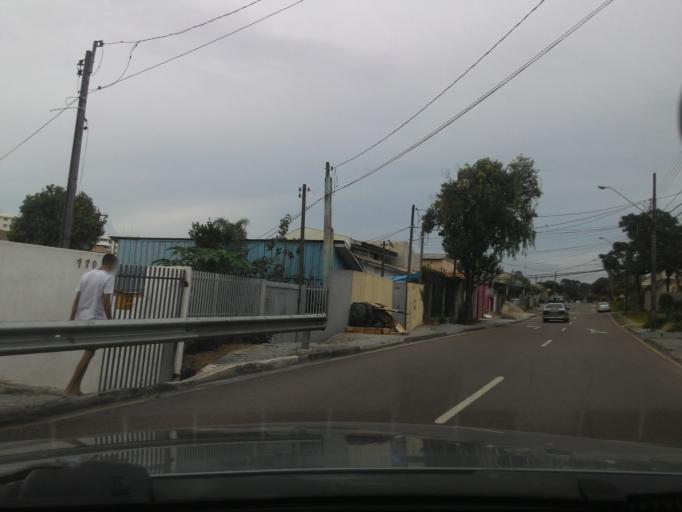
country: BR
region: Parana
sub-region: Pinhais
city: Pinhais
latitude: -25.4468
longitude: -49.2244
